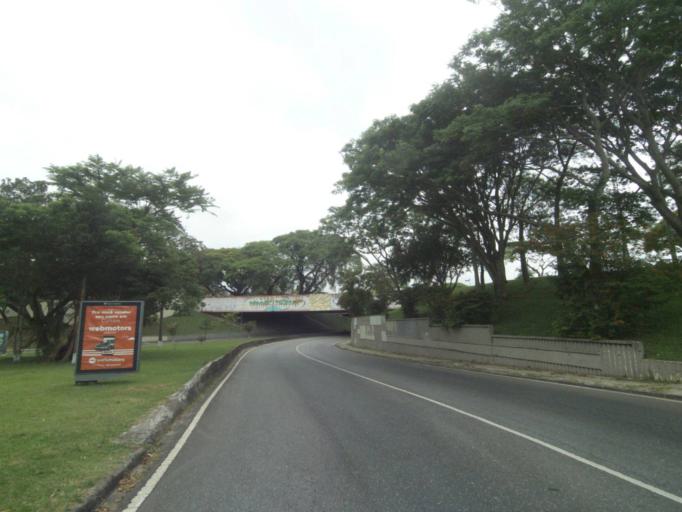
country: BR
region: Parana
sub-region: Curitiba
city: Curitiba
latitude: -25.4281
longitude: -49.2425
